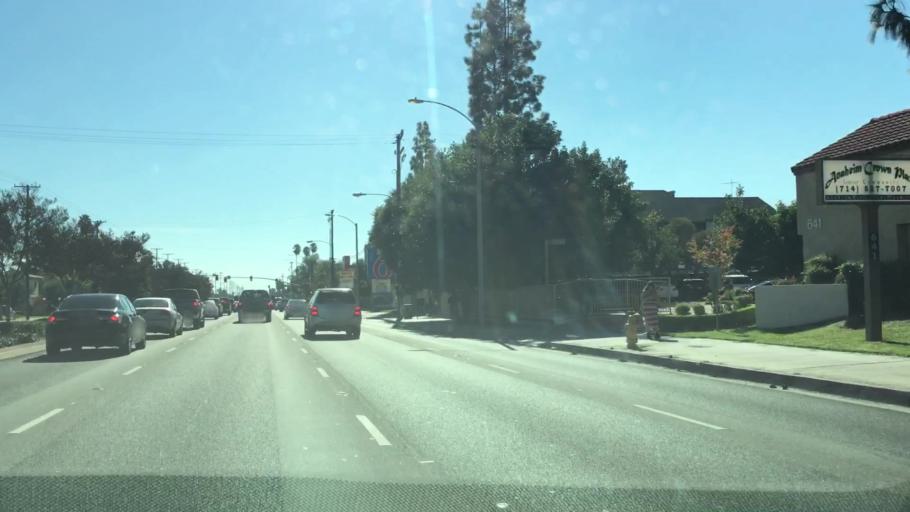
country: US
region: California
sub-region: Orange County
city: Stanton
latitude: 33.8234
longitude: -117.9934
